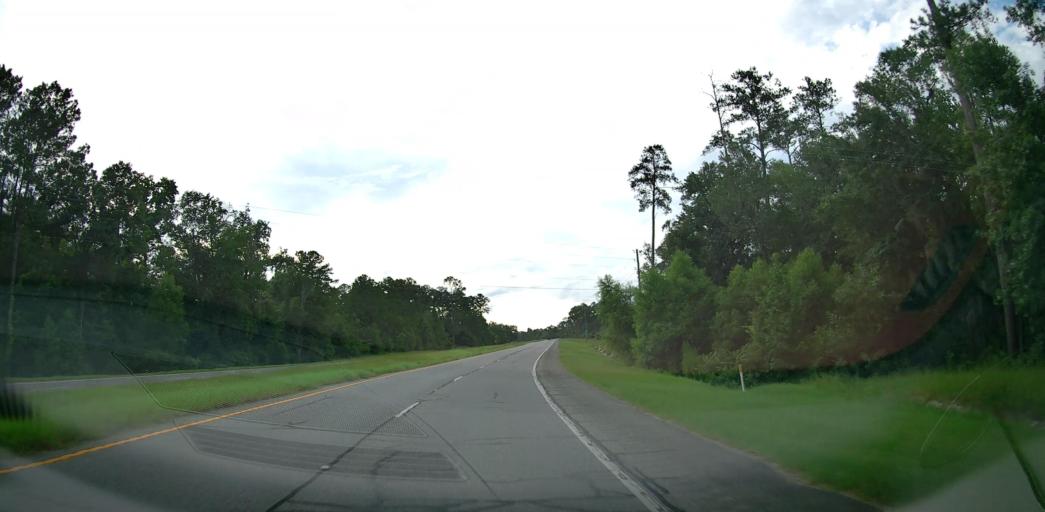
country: US
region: Georgia
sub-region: Pulaski County
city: Hawkinsville
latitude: 32.2635
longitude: -83.4090
